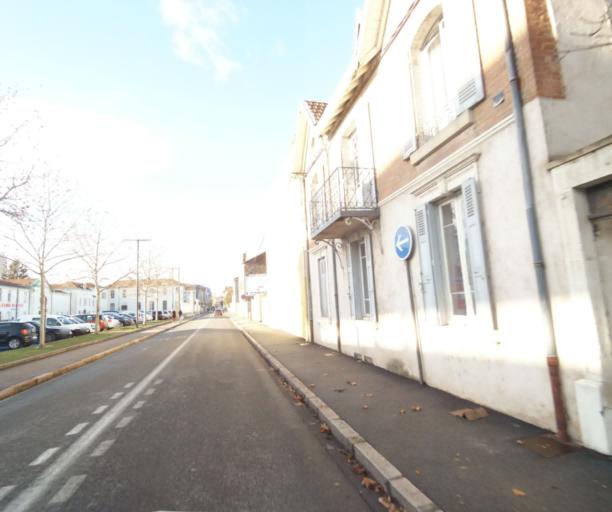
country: FR
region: Rhone-Alpes
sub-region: Departement de la Loire
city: Roanne
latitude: 46.0425
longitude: 4.0771
